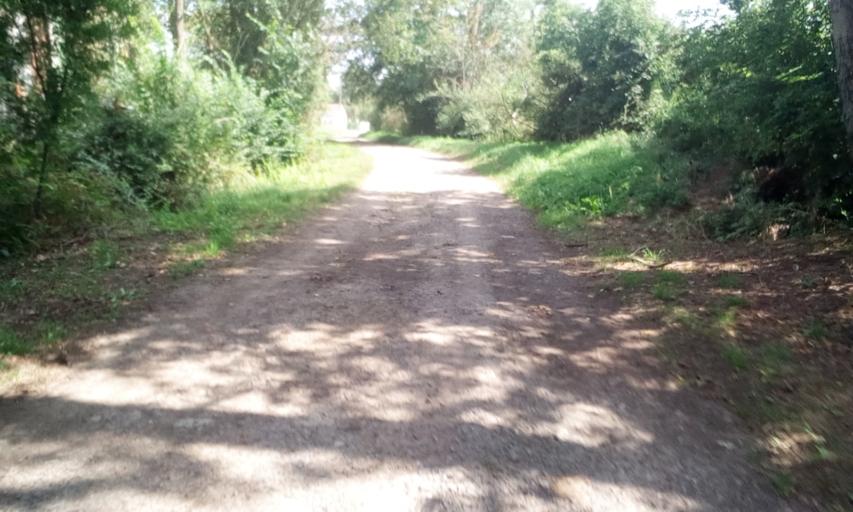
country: FR
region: Lower Normandy
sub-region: Departement du Calvados
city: Argences
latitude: 49.1453
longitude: -0.1503
